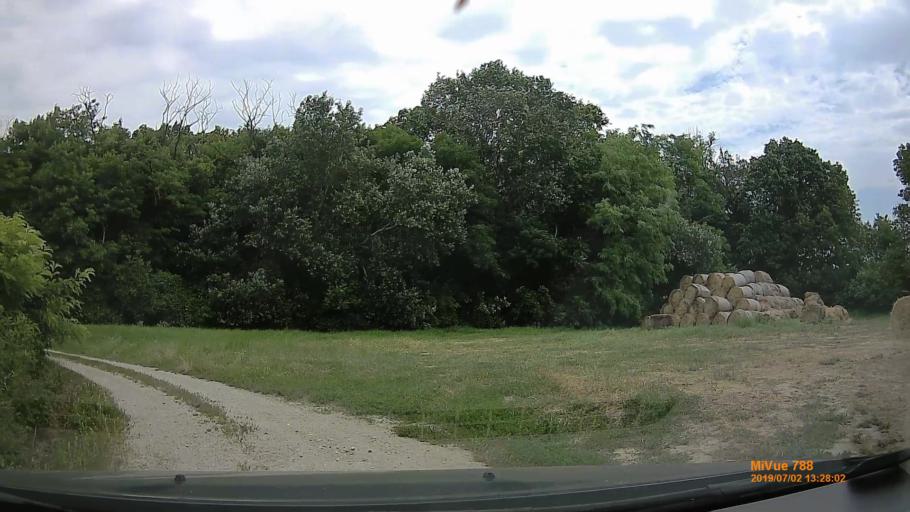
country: HU
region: Gyor-Moson-Sopron
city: Halaszi
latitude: 47.8631
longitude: 17.3228
